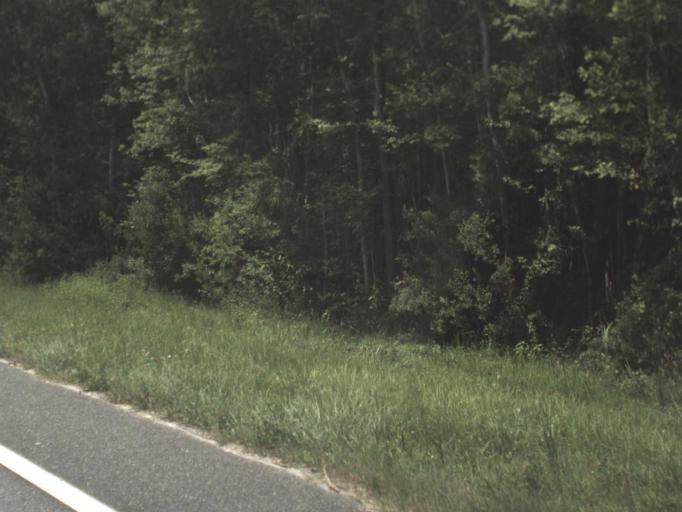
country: US
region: Georgia
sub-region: Echols County
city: Statenville
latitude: 30.5757
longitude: -83.0830
